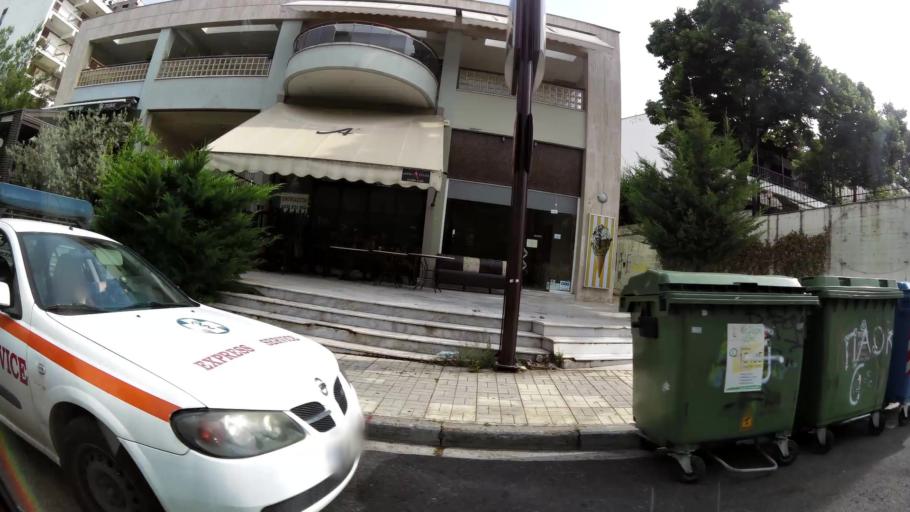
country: GR
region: Central Macedonia
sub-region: Nomos Thessalonikis
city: Panorama
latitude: 40.5915
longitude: 23.0333
